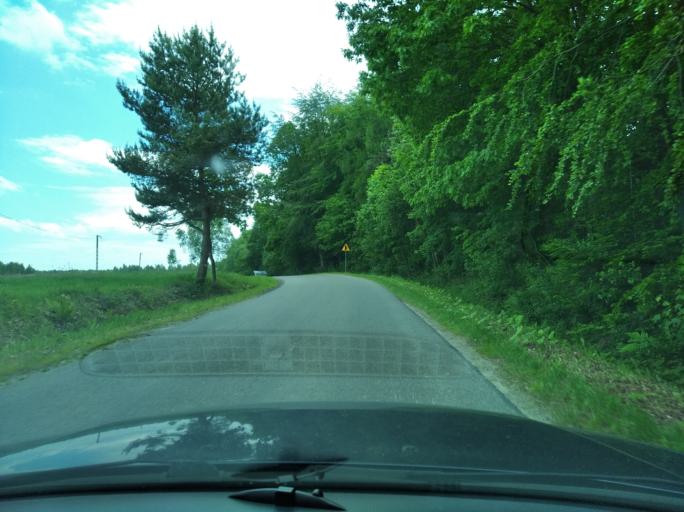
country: PL
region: Subcarpathian Voivodeship
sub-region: Powiat ropczycko-sedziszowski
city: Ropczyce
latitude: 50.0168
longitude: 21.6090
